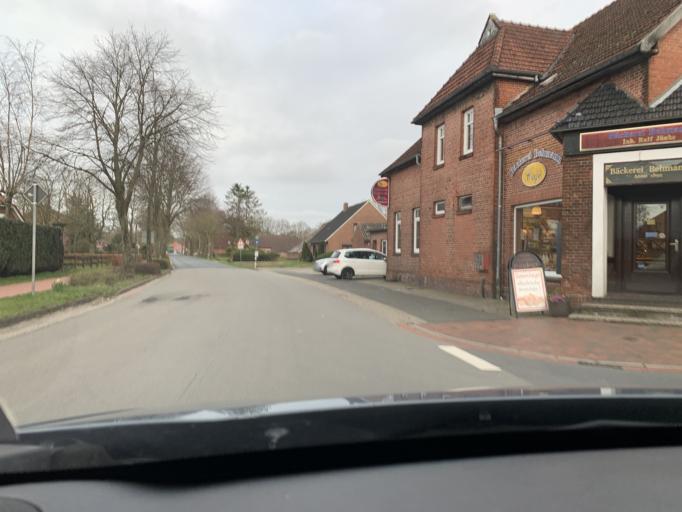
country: DE
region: Lower Saxony
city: Detern
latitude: 53.2545
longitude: 7.7105
